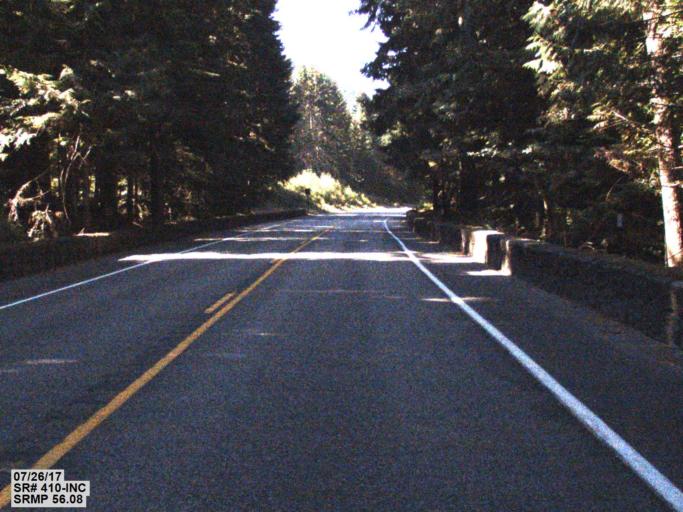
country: US
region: Washington
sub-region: King County
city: Enumclaw
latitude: 46.9999
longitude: -121.5289
